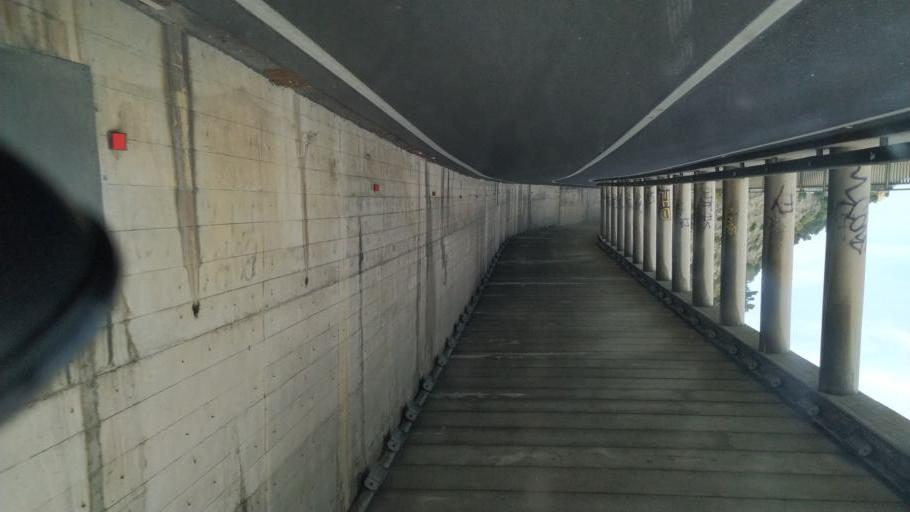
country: IT
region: Liguria
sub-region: Provincia di Savona
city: Laigueglia
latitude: 43.9639
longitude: 8.1666
